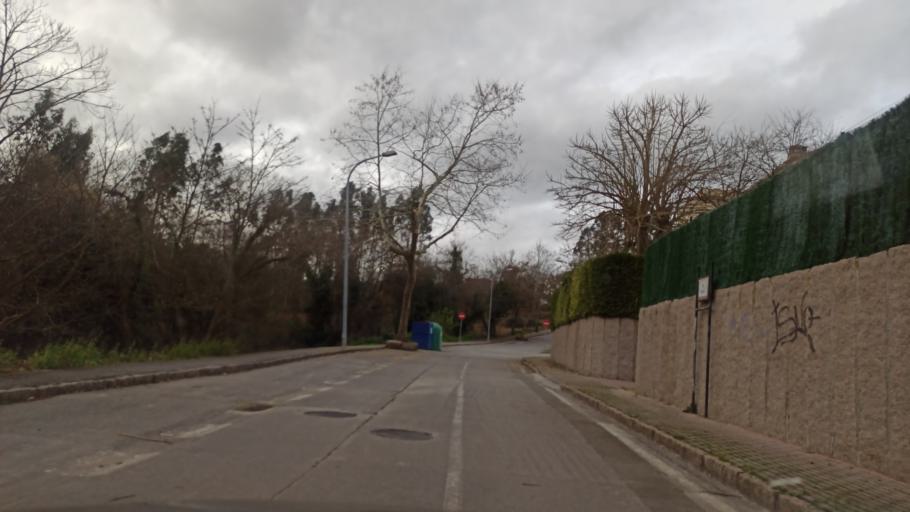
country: ES
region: Galicia
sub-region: Provincia da Coruna
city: Cambre
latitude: 43.3267
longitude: -8.3486
